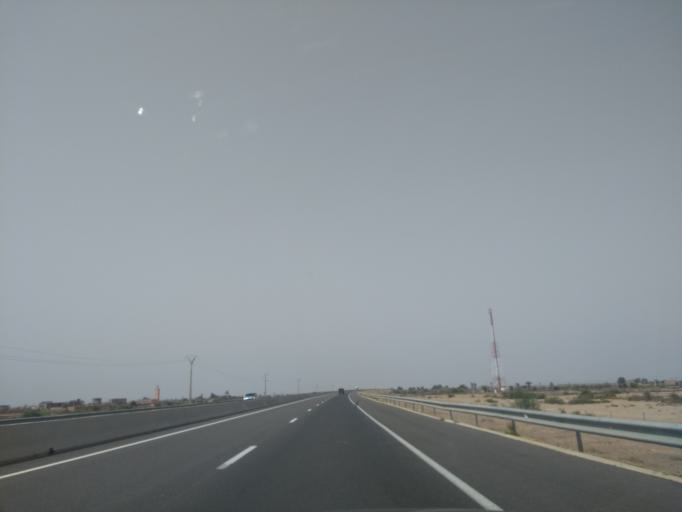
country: MA
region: Marrakech-Tensift-Al Haouz
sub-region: Marrakech
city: Marrakesh
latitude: 31.6794
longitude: -8.2777
